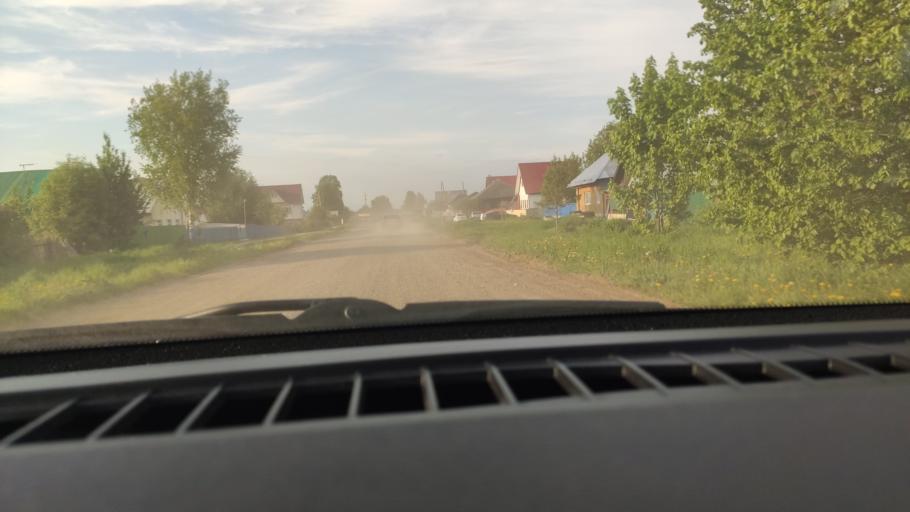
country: RU
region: Perm
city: Kultayevo
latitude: 57.9193
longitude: 56.0039
